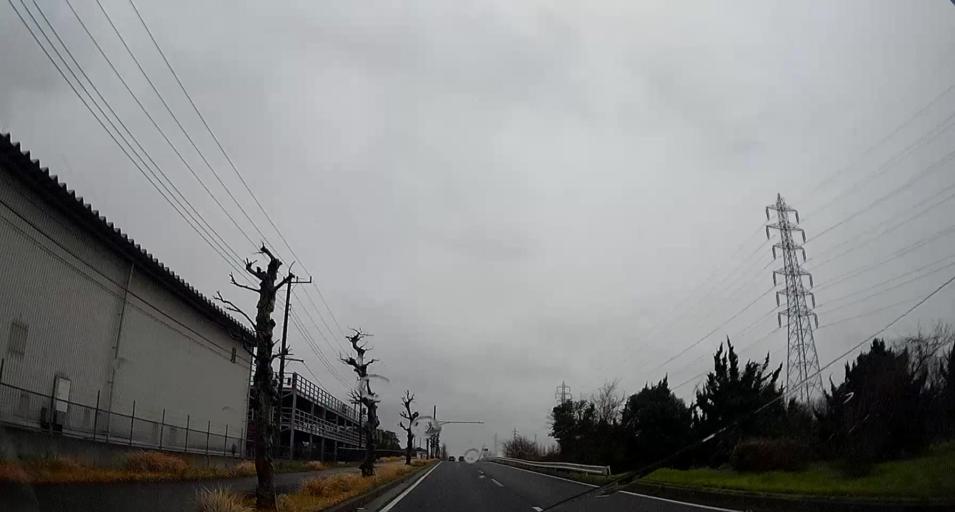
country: JP
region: Chiba
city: Ichihara
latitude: 35.5069
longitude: 140.0534
